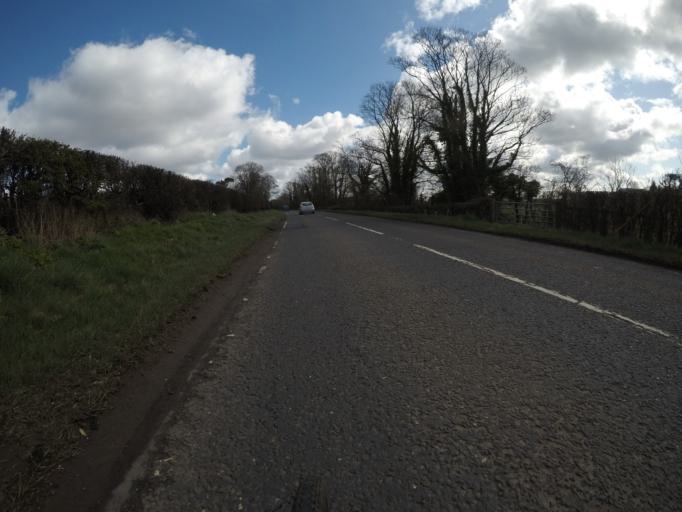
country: GB
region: Scotland
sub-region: South Ayrshire
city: Dundonald
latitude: 55.5863
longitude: -4.5695
